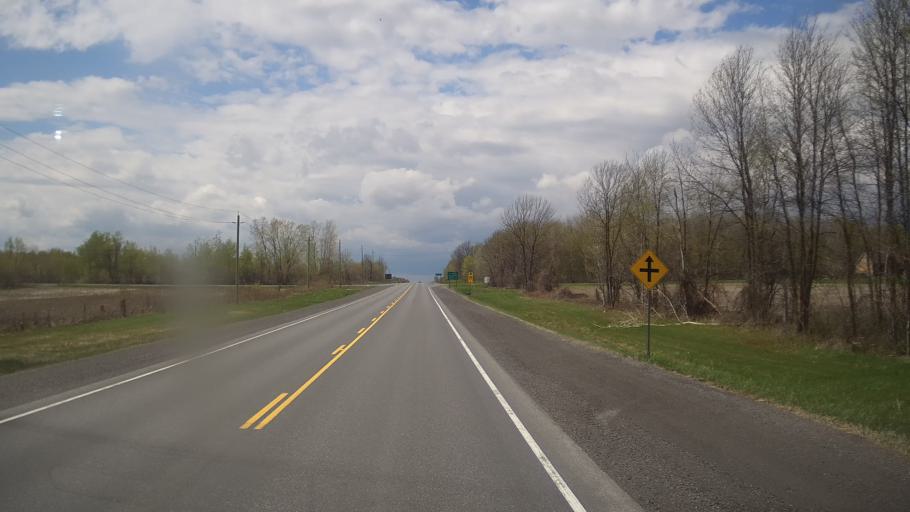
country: CA
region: Ontario
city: Hawkesbury
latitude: 45.5707
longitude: -74.5209
